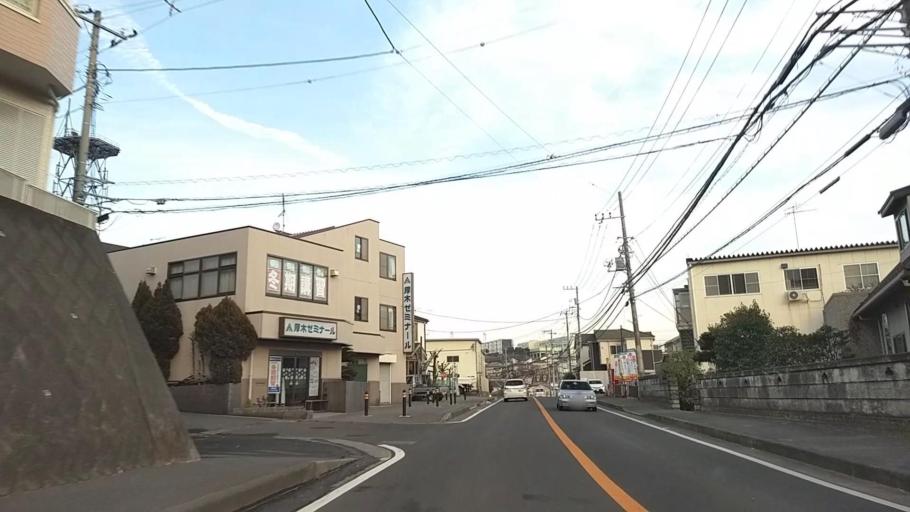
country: JP
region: Kanagawa
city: Atsugi
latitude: 35.4400
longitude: 139.3245
